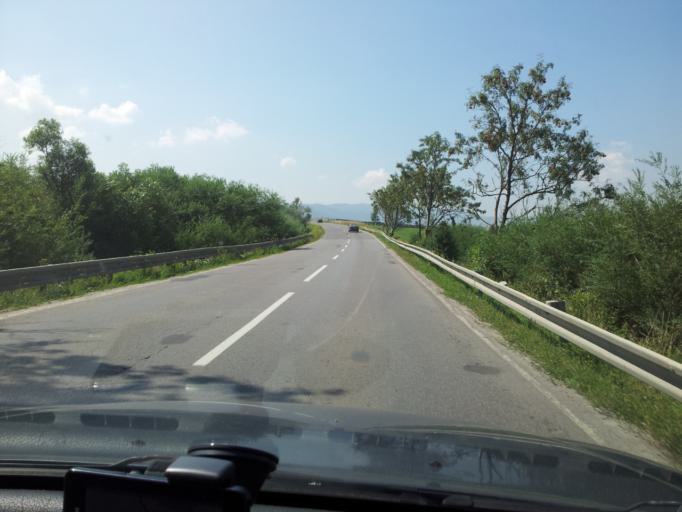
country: SK
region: Zilinsky
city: Namestovo
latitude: 49.3540
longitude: 19.3962
